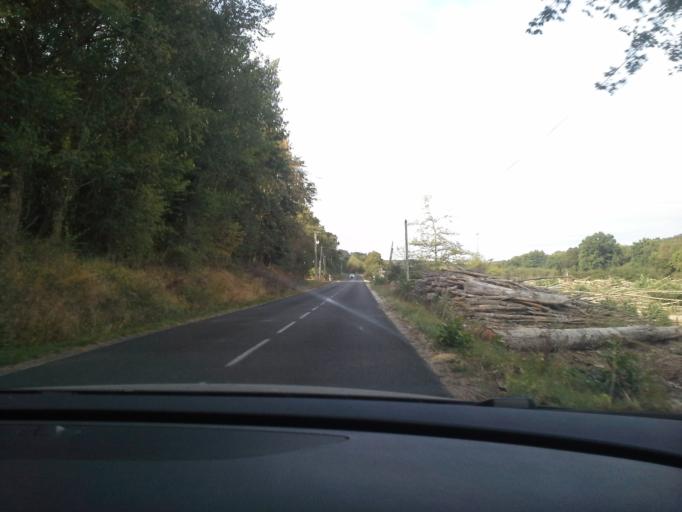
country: FR
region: Centre
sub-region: Departement d'Indre-et-Loire
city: Auzouer-en-Touraine
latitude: 47.5313
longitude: 0.9164
